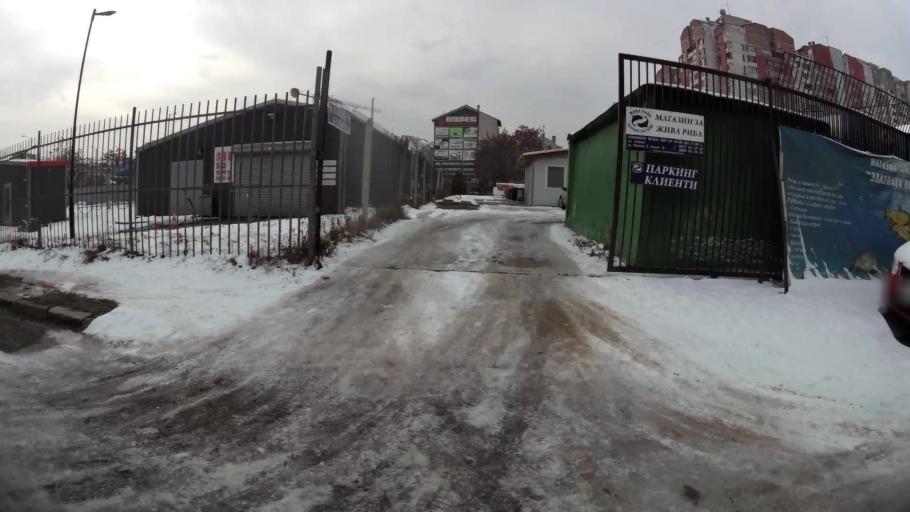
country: BG
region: Sofia-Capital
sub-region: Stolichna Obshtina
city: Sofia
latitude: 42.7065
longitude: 23.3048
